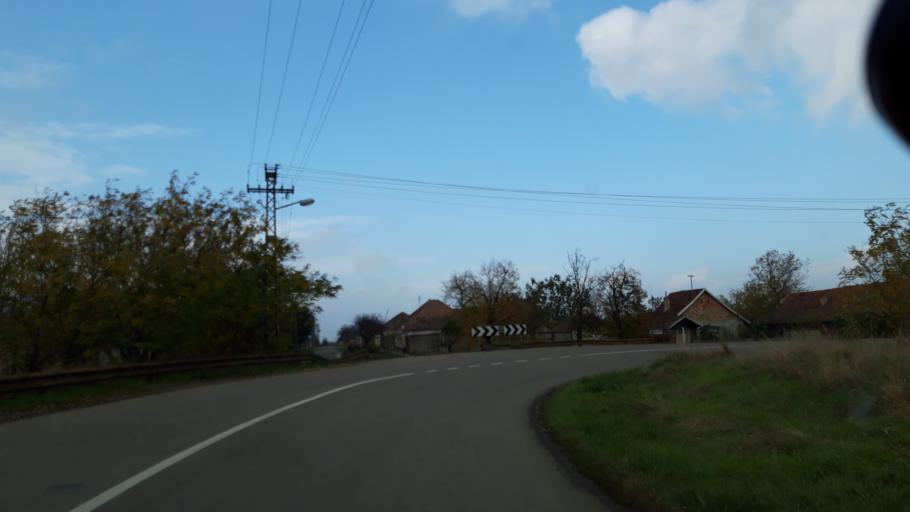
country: RS
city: Padej
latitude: 45.8205
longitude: 20.1575
